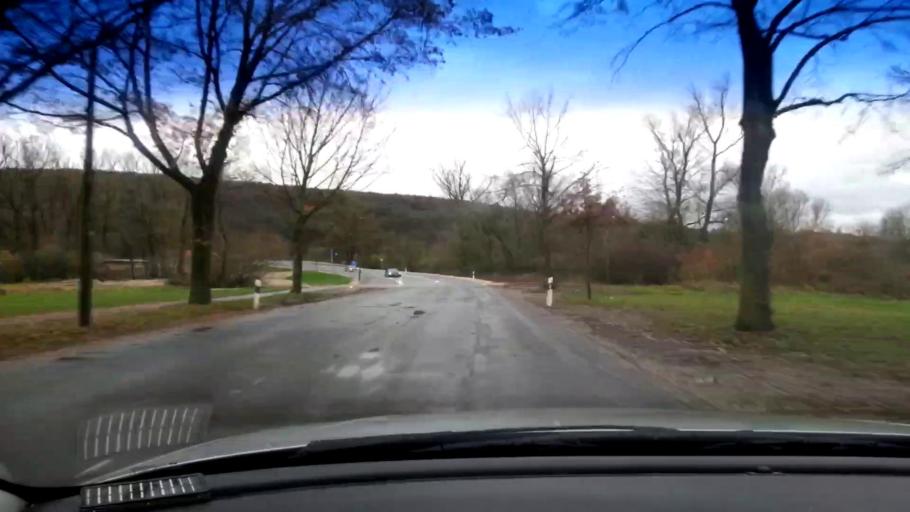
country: DE
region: Bavaria
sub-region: Upper Franconia
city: Rattelsdorf
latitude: 50.0033
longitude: 10.9105
